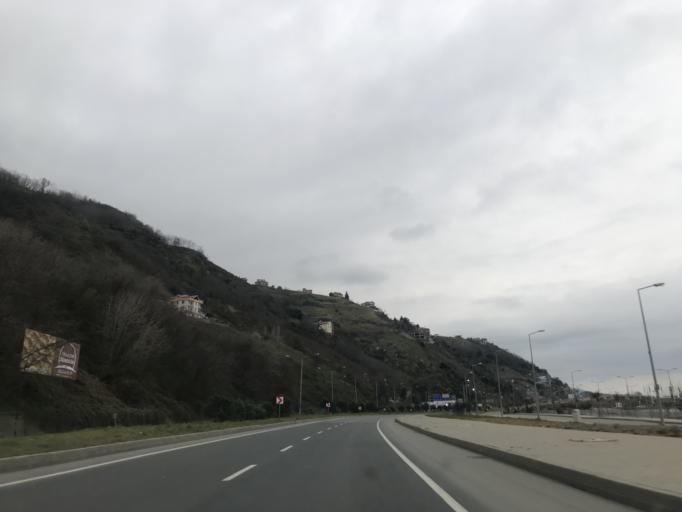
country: TR
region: Trabzon
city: Derecik
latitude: 40.9958
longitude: 39.6471
